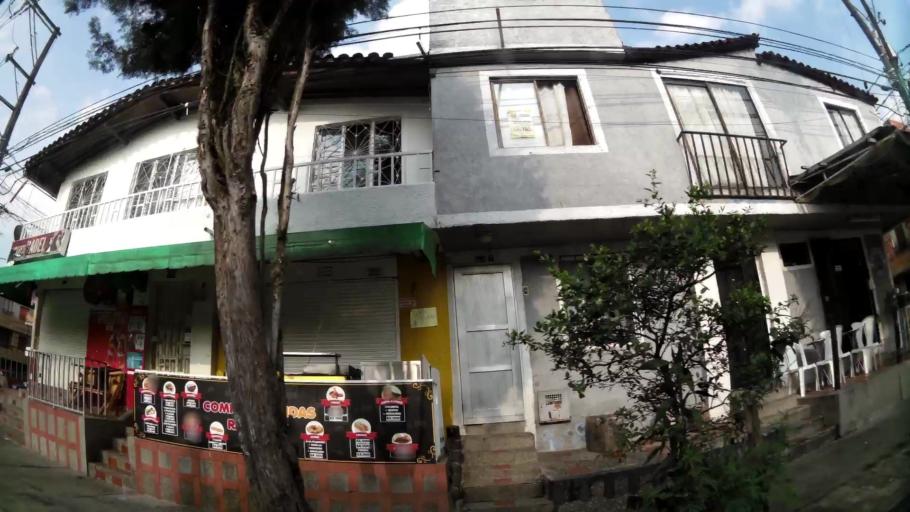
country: CO
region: Antioquia
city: Sabaneta
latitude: 6.1629
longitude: -75.6266
